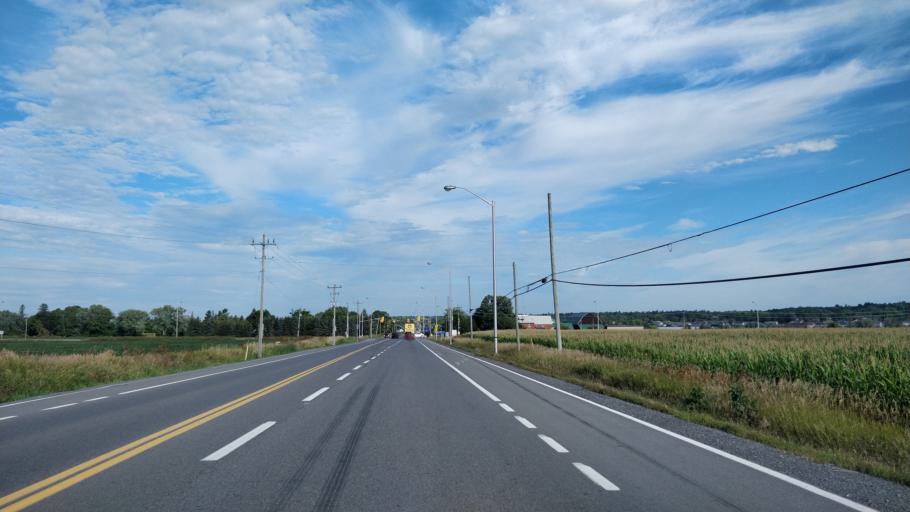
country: CA
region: Ontario
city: Bells Corners
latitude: 45.3329
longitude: -76.0213
